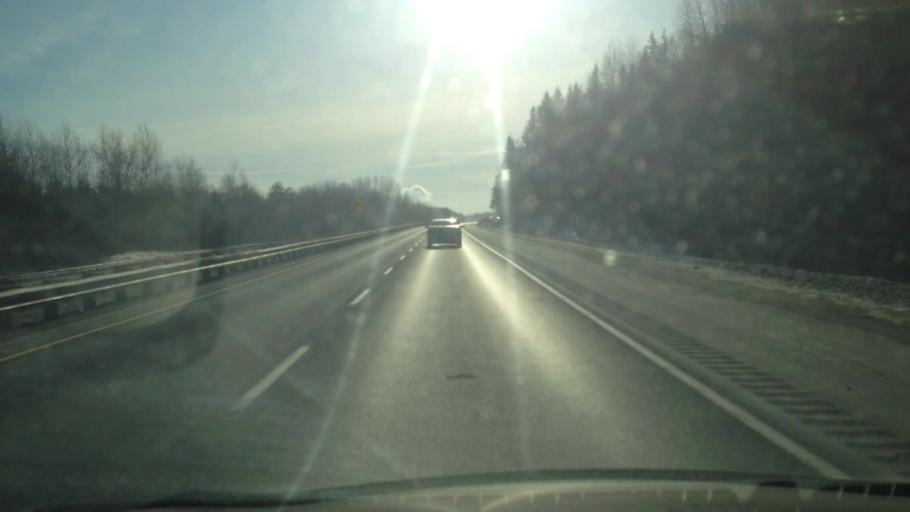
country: CA
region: Quebec
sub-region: Laurentides
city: Prevost
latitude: 45.8531
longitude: -74.0762
